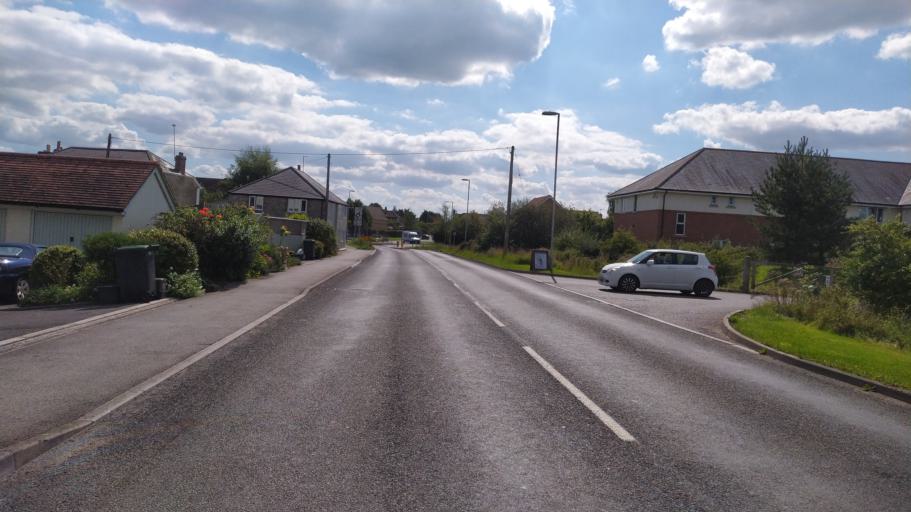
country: GB
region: England
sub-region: Dorset
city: Gillingham
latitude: 51.0498
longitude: -2.2817
